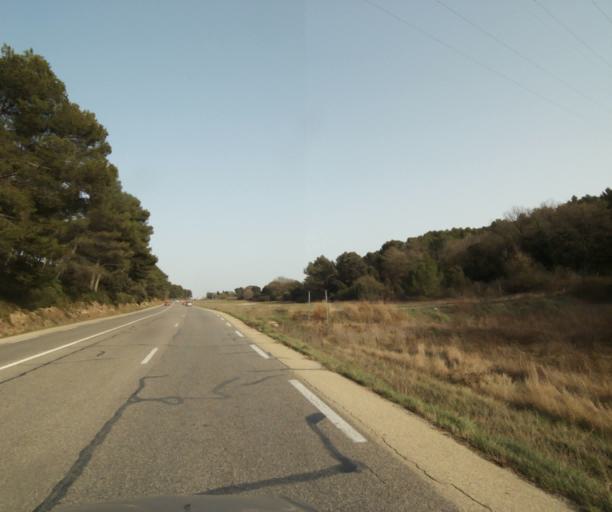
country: FR
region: Provence-Alpes-Cote d'Azur
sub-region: Departement des Bouches-du-Rhone
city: Les Pennes-Mirabeau
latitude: 43.4132
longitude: 5.3410
